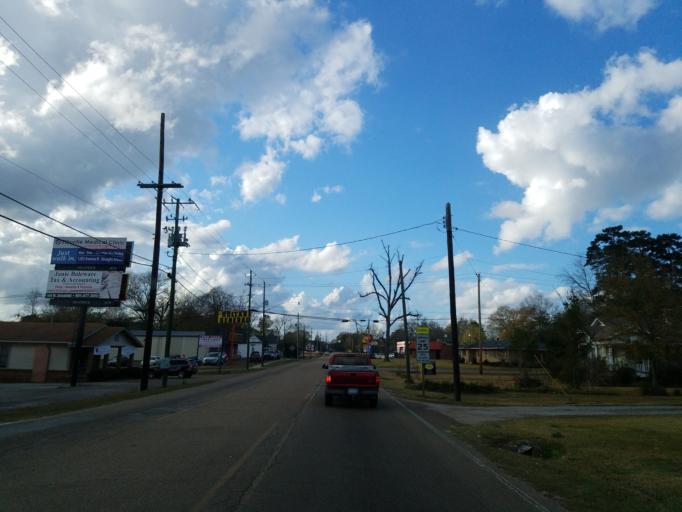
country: US
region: Mississippi
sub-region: Jones County
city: Ellisville
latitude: 31.6062
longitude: -89.1977
